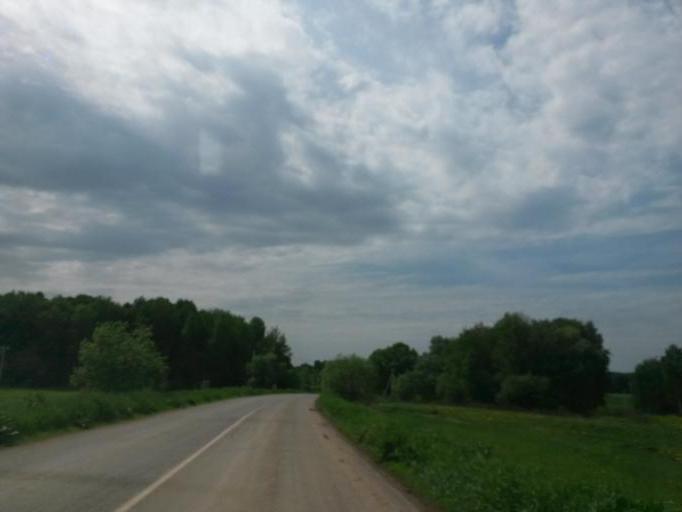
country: RU
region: Moskovskaya
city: Melikhovo
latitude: 55.1669
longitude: 37.6994
